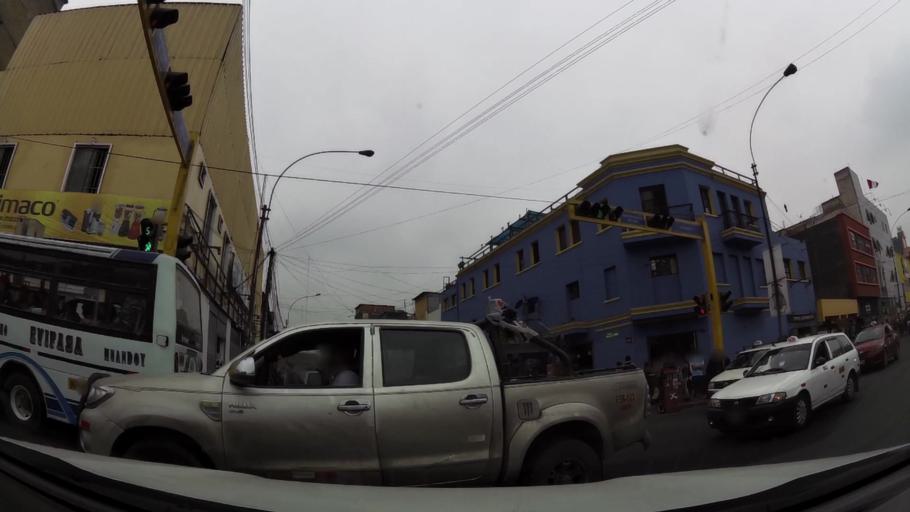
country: PE
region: Lima
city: Lima
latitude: -12.0566
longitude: -77.0301
